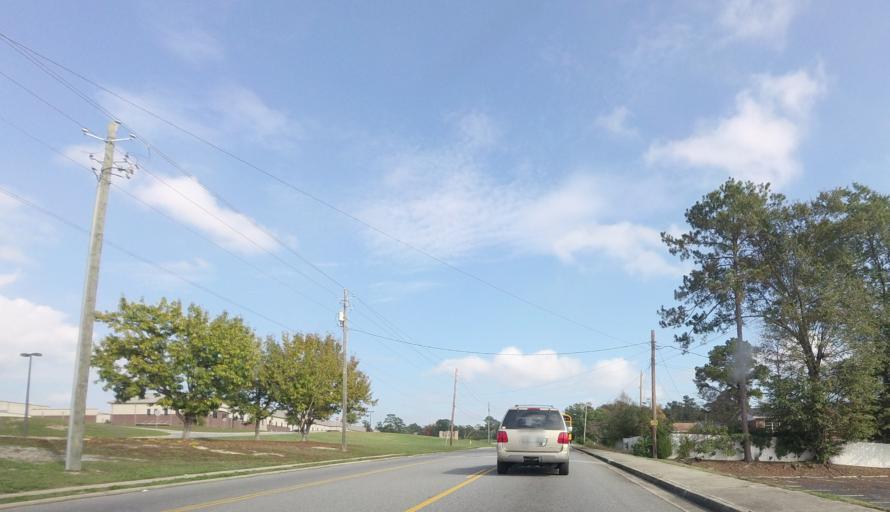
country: US
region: Georgia
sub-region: Bibb County
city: Macon
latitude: 32.8060
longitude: -83.6751
